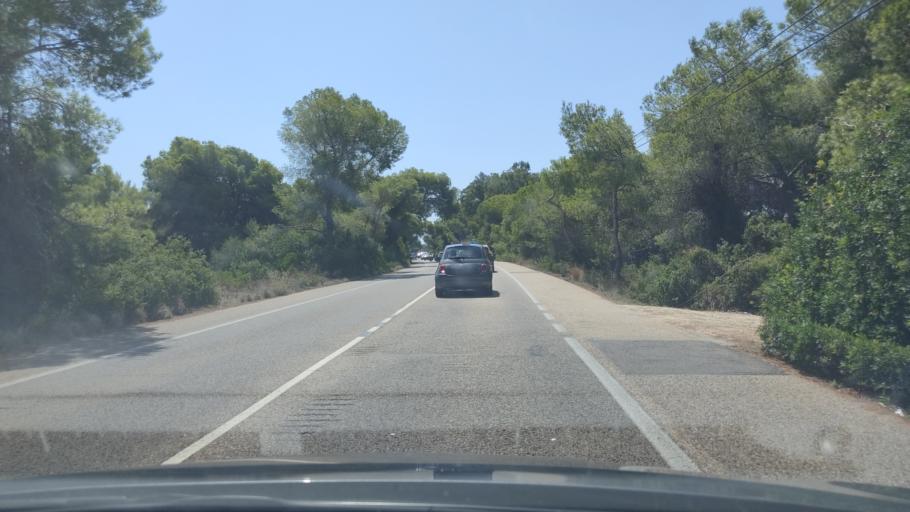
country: ES
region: Valencia
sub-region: Provincia de Valencia
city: Sollana
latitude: 39.3244
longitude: -0.3102
